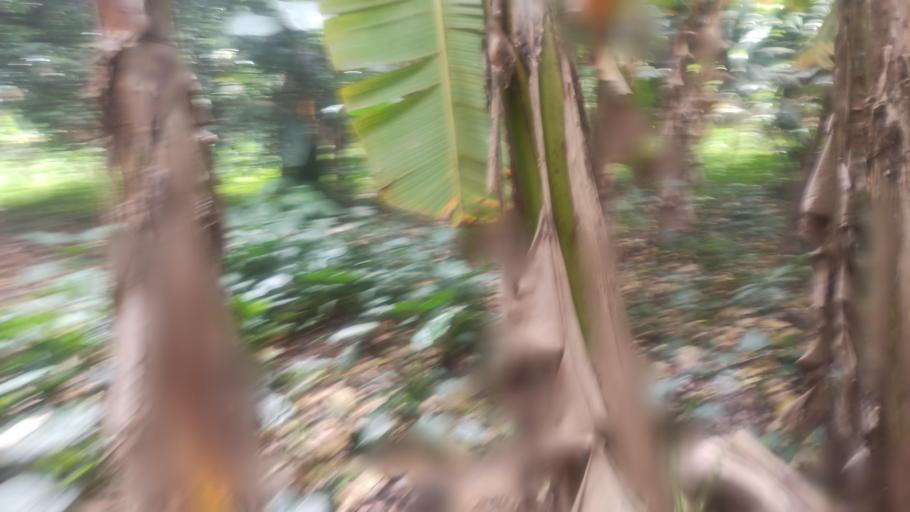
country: CO
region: Cauca
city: Puerto Tejada
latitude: 3.2667
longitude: -76.4675
